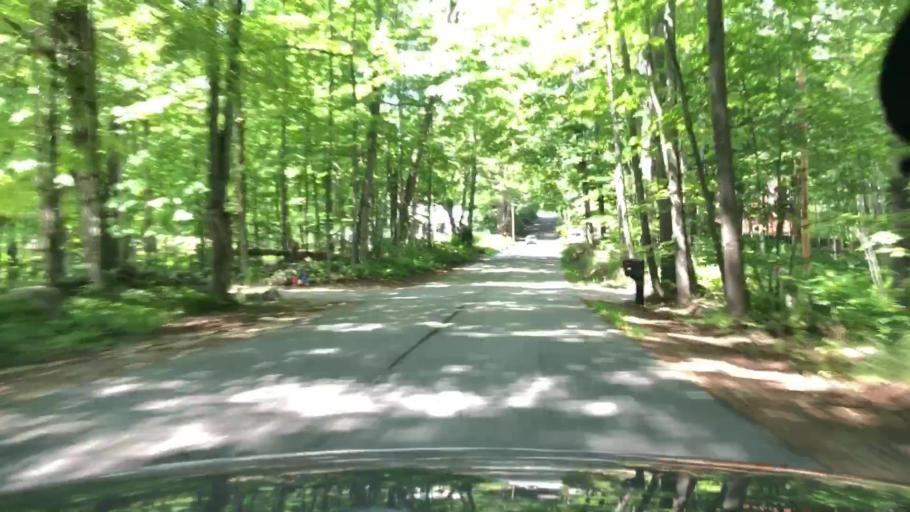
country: US
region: New Hampshire
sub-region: Grafton County
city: Holderness
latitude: 43.7235
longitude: -71.5652
